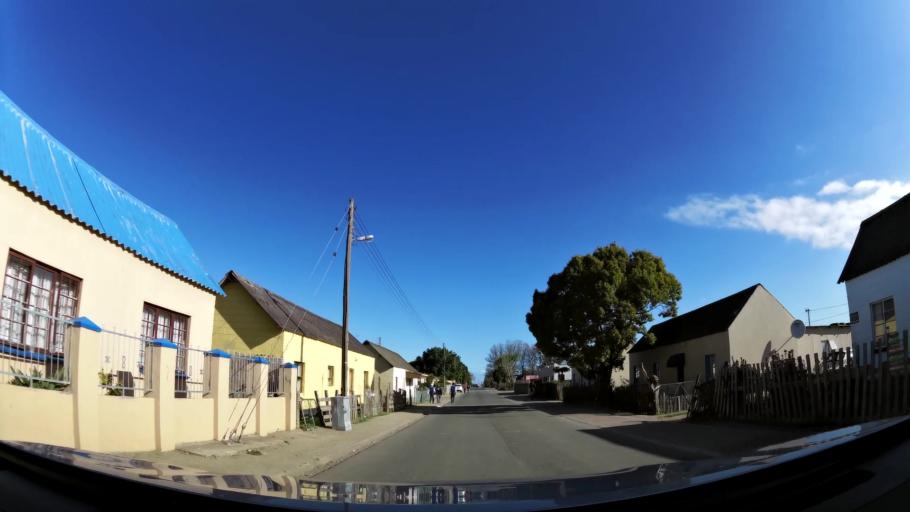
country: ZA
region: Western Cape
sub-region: Eden District Municipality
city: George
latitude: -33.9709
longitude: 22.4799
